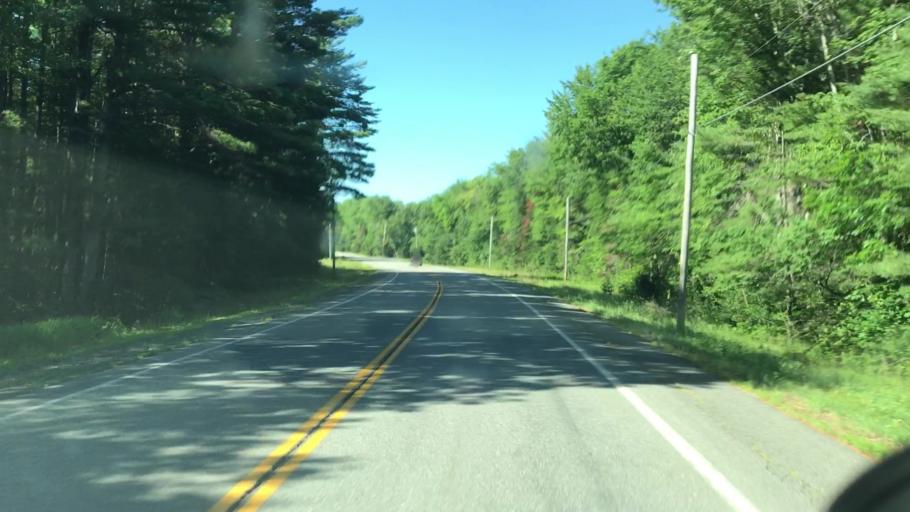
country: US
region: Maine
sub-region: Penobscot County
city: Howland
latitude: 45.2727
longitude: -68.6374
